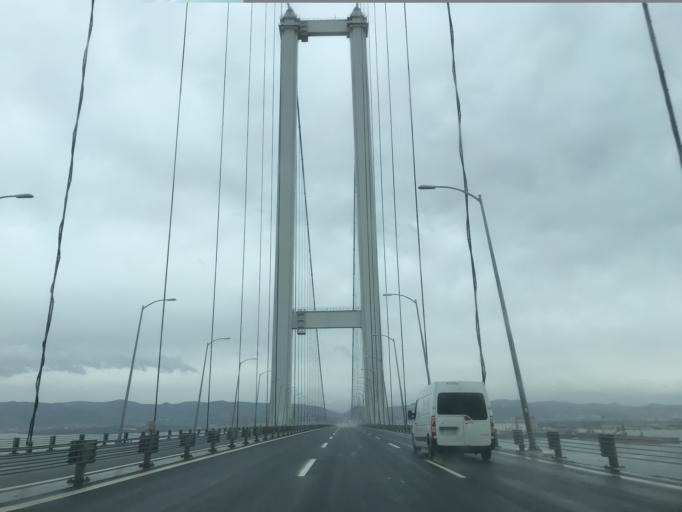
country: TR
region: Yalova
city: Altinova
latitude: 40.7502
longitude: 29.5150
